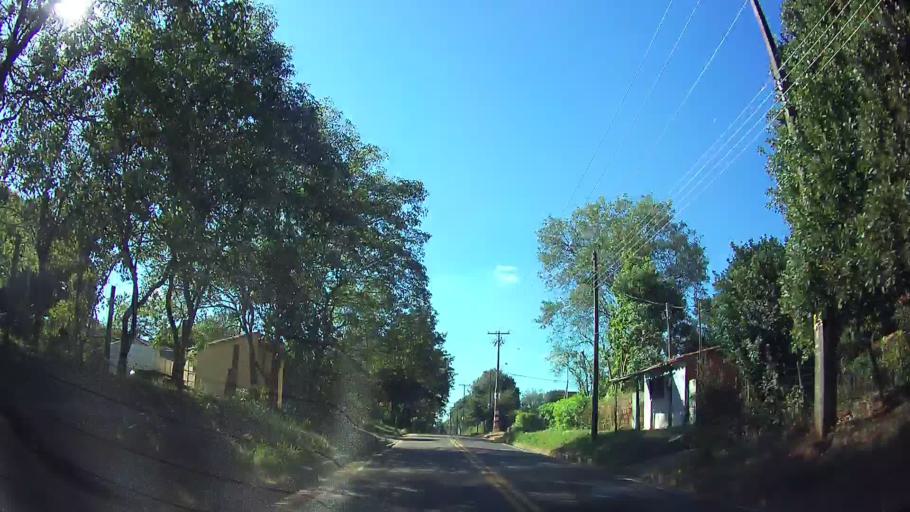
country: PY
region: Central
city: Limpio
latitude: -25.2053
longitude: -57.4799
